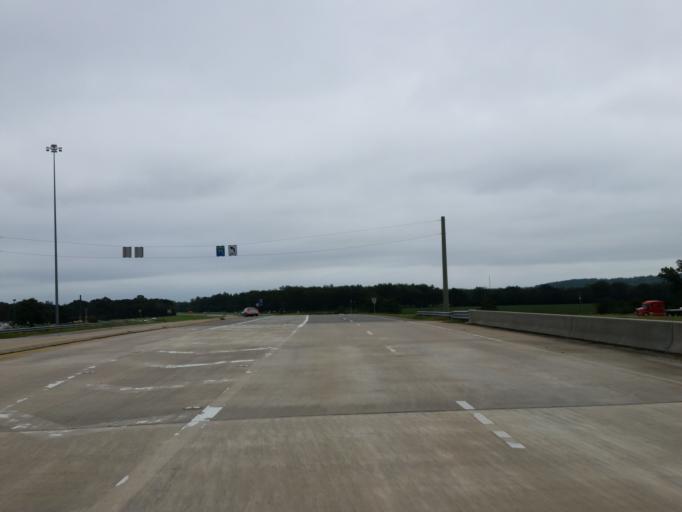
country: US
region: Georgia
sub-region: Houston County
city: Perry
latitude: 32.4315
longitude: -83.7570
